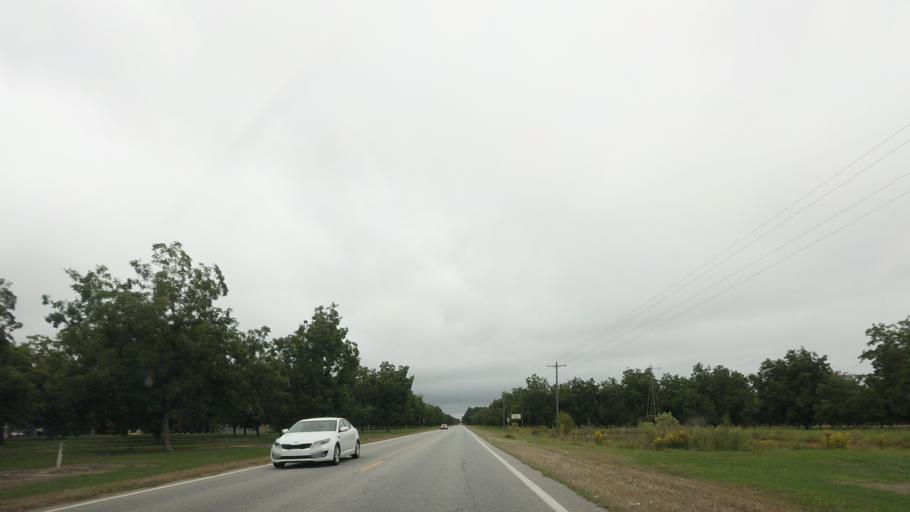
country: US
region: Georgia
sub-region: Berrien County
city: Ray City
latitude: 31.0922
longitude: -83.2061
